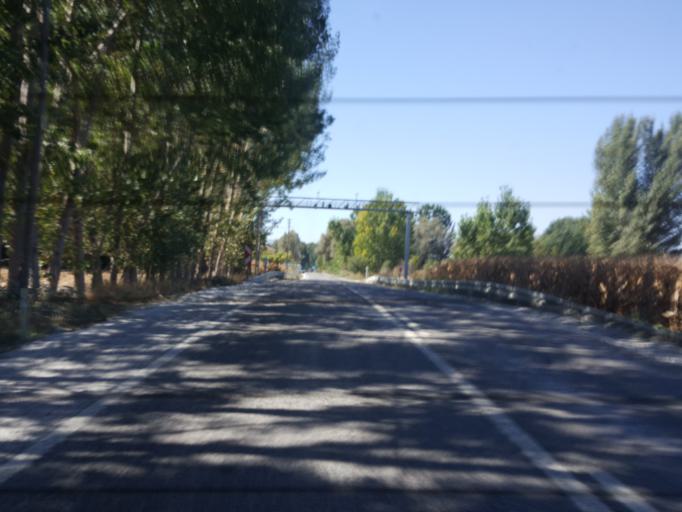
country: TR
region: Tokat
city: Pazar
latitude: 40.2734
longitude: 36.2600
